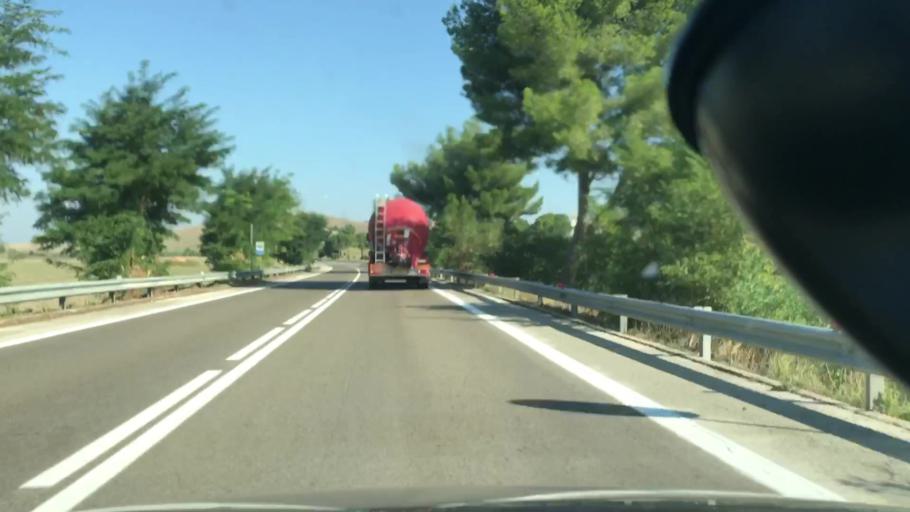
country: IT
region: Basilicate
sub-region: Provincia di Matera
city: Irsina
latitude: 40.8038
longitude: 16.2738
